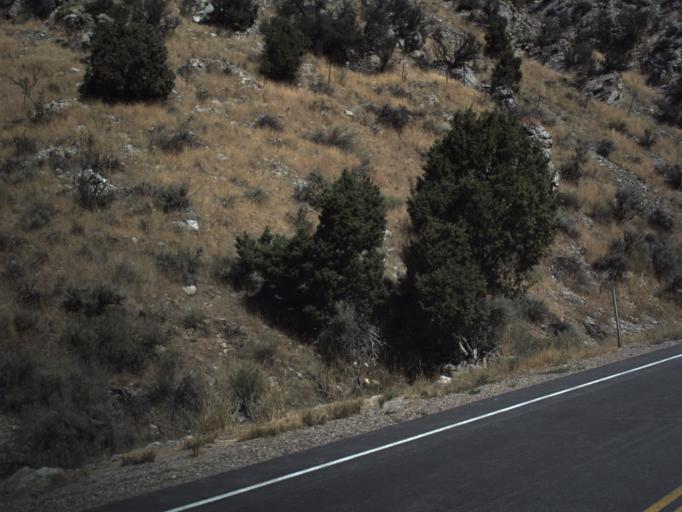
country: US
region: Utah
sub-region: Rich County
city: Randolph
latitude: 41.8244
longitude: -111.2953
